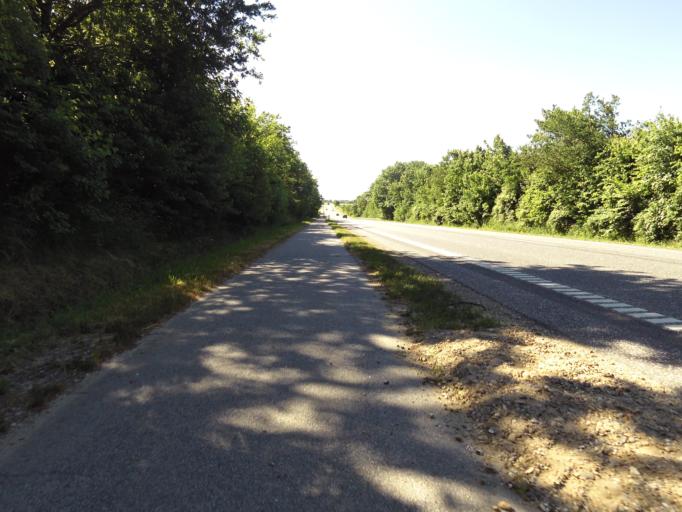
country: DK
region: Central Jutland
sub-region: Struer Kommune
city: Struer
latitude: 56.4607
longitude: 8.5900
